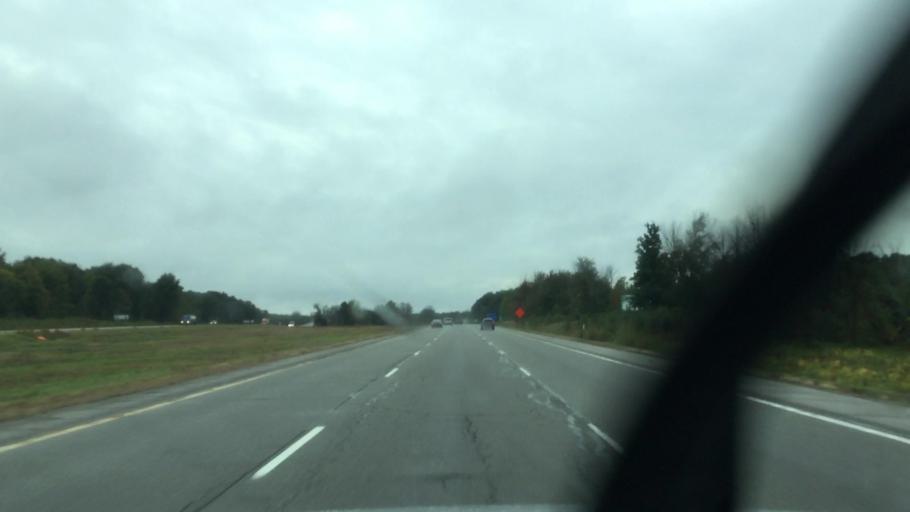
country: US
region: Michigan
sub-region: Berrien County
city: New Buffalo
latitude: 41.8119
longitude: -86.6972
